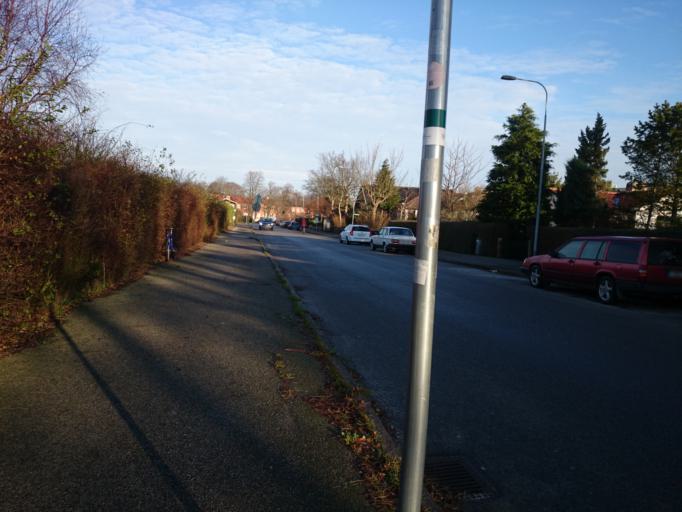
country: SE
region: Skane
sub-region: Lunds Kommun
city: Lund
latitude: 55.6933
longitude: 13.2000
